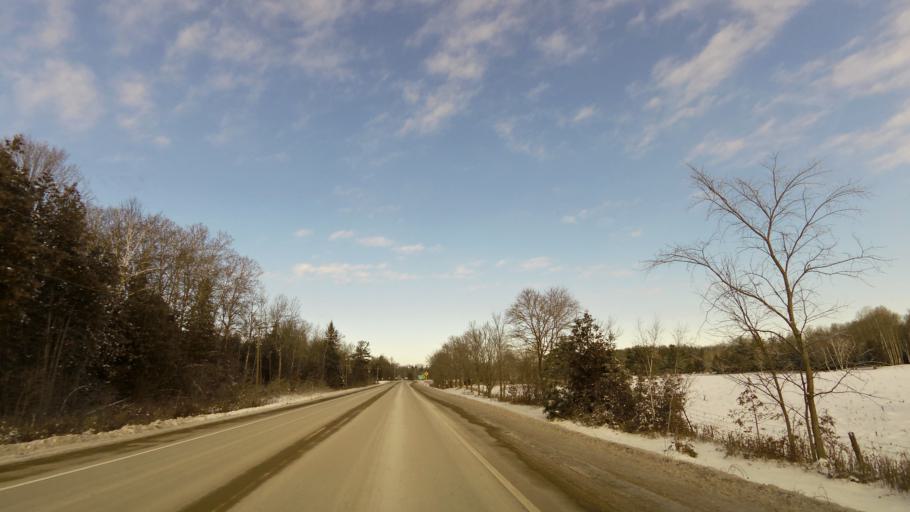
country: CA
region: Ontario
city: Quinte West
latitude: 44.1242
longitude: -77.7838
